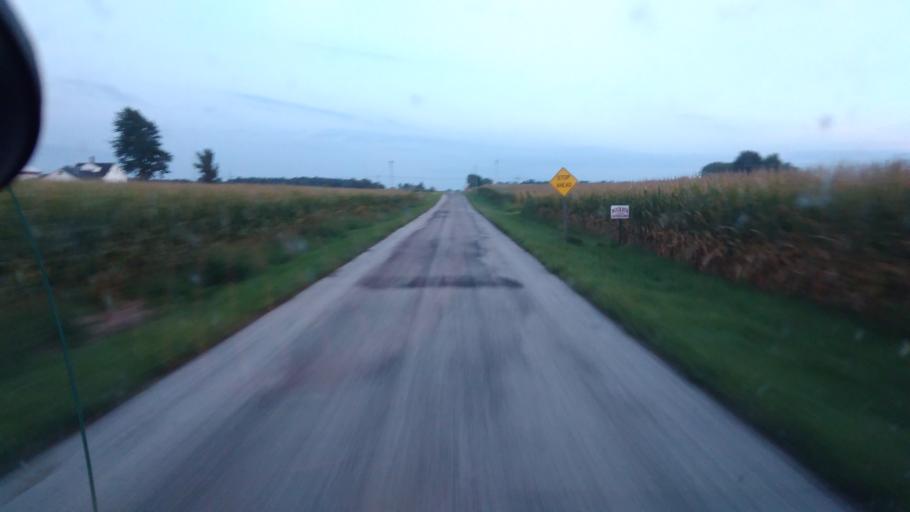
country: US
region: Ohio
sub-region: Hardin County
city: Kenton
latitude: 40.6457
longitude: -83.4581
